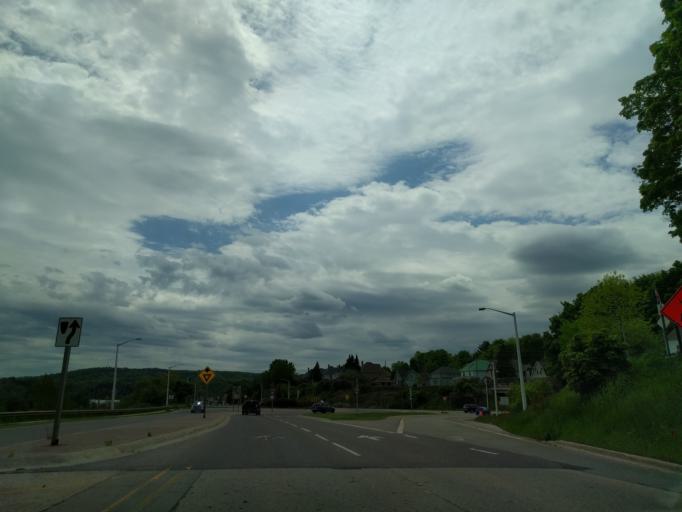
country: US
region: Michigan
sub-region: Marquette County
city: Marquette
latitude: 46.5384
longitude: -87.3945
